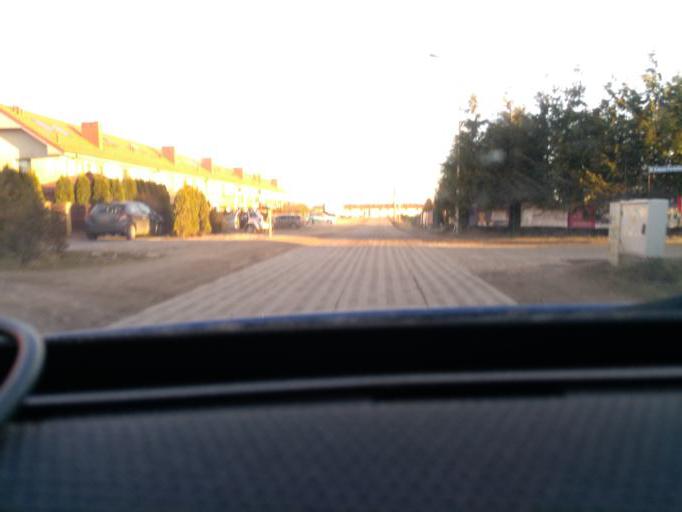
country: PL
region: Pomeranian Voivodeship
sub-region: Powiat kartuski
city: Banino
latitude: 54.3872
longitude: 18.3841
